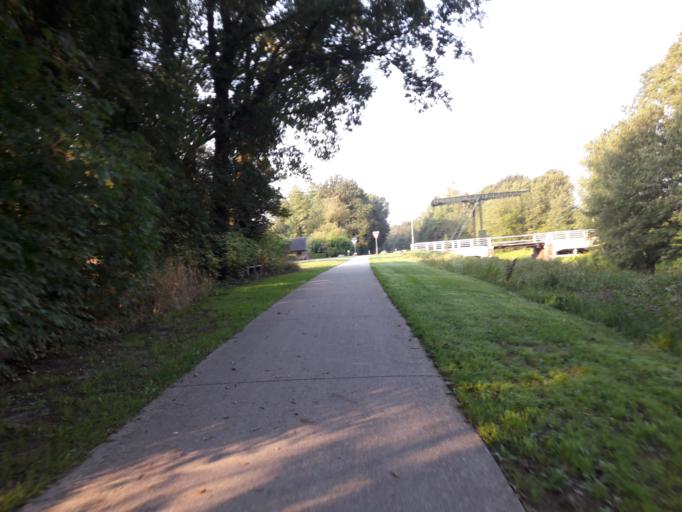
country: NL
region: Drenthe
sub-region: Gemeente Borger-Odoorn
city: Borger
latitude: 52.9063
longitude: 6.7646
